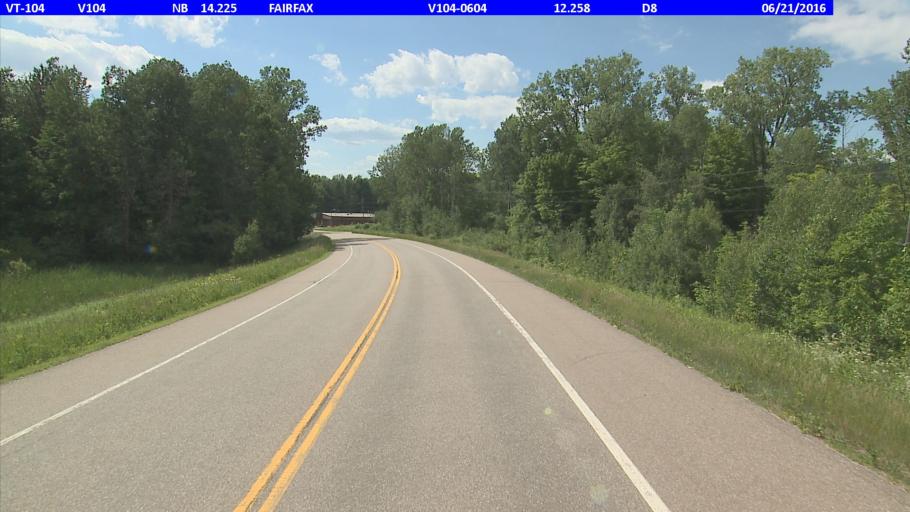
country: US
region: Vermont
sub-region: Franklin County
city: Saint Albans
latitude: 44.7599
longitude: -73.0586
